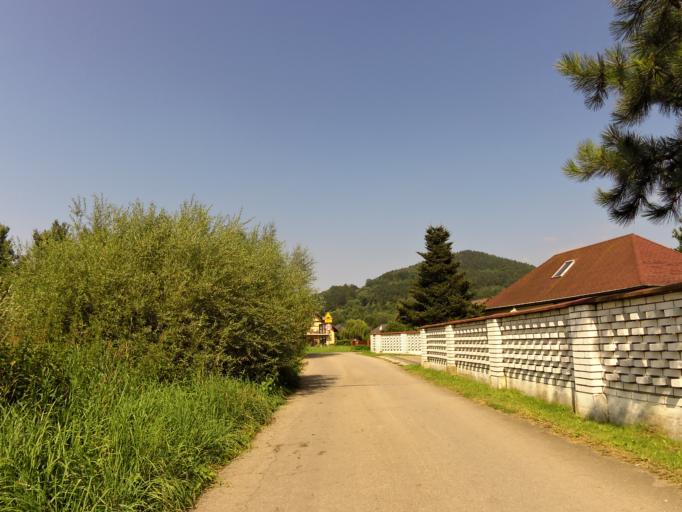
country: PL
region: Silesian Voivodeship
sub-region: Powiat zywiecki
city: Wieprz
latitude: 49.6500
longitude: 19.1789
